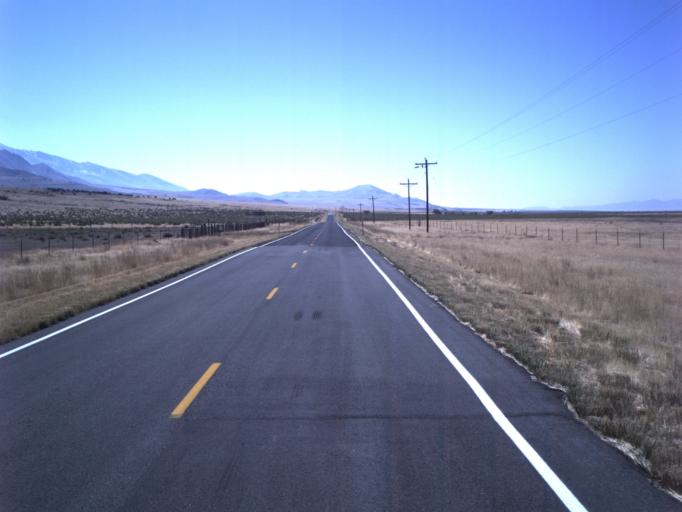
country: US
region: Utah
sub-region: Tooele County
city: Grantsville
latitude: 40.6861
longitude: -112.6697
